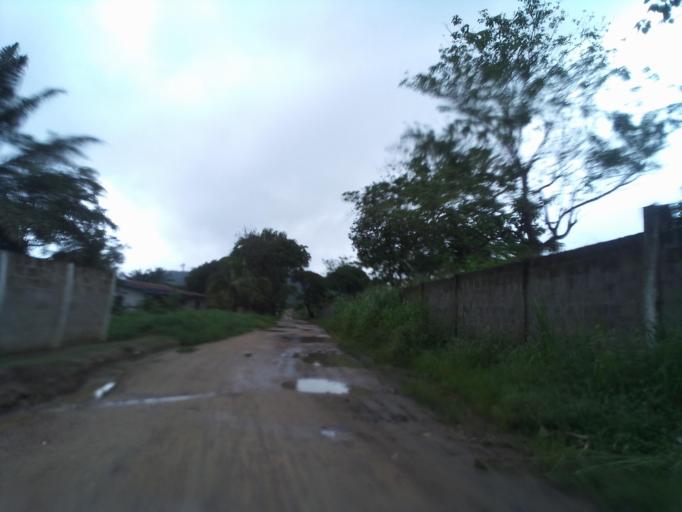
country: SL
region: Eastern Province
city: Kenema
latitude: 7.8535
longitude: -11.2078
